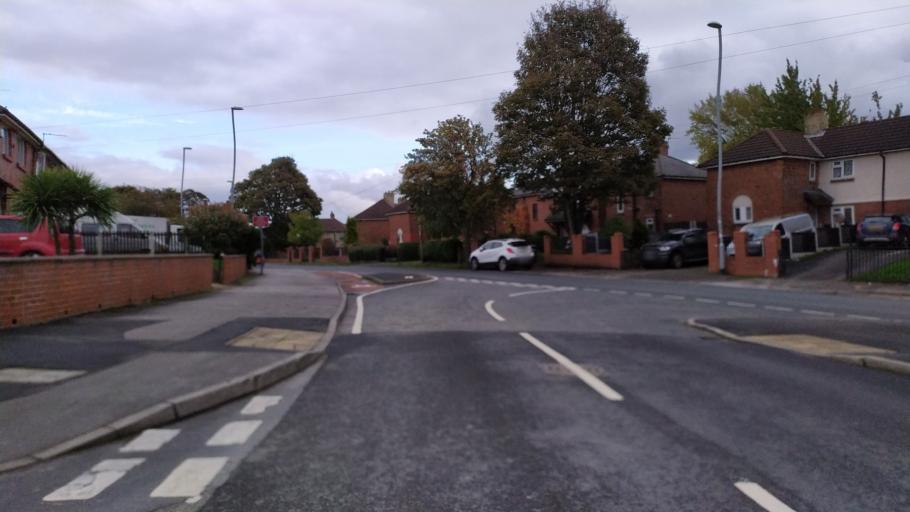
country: GB
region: England
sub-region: City and Borough of Leeds
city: Chapel Allerton
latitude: 53.8252
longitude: -1.5516
